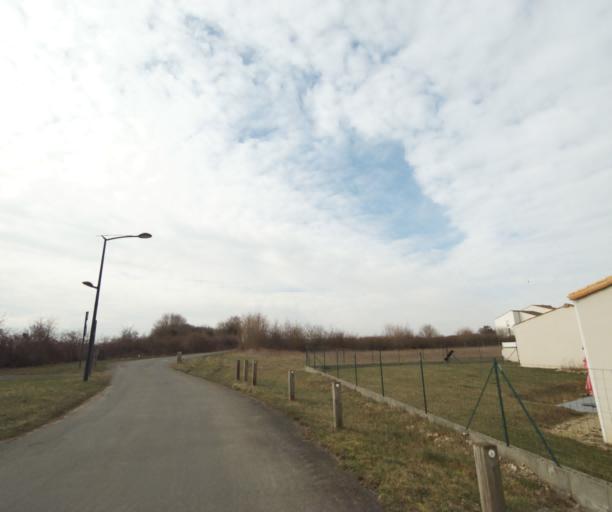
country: FR
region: Poitou-Charentes
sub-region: Departement des Deux-Sevres
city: Aiffres
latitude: 46.3130
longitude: -0.4305
